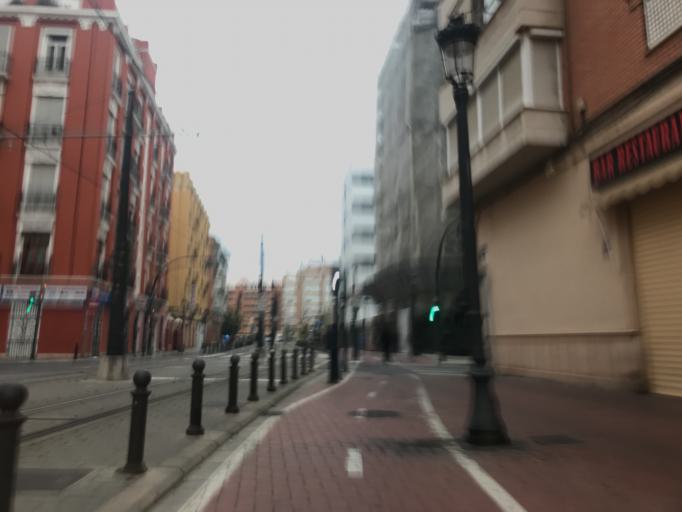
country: ES
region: Valencia
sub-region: Provincia de Valencia
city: Alboraya
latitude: 39.4636
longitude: -0.3346
